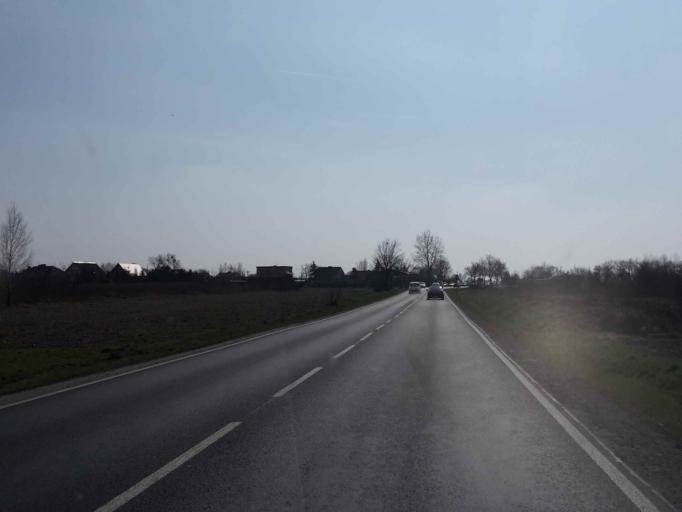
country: PL
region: Kujawsko-Pomorskie
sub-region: Powiat torunski
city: Lubicz Dolny
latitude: 53.0747
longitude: 18.7619
